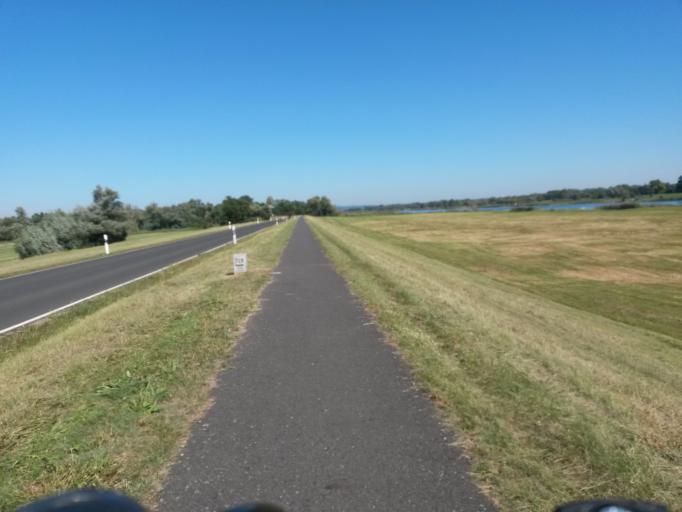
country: PL
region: West Pomeranian Voivodeship
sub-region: Powiat gryfinski
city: Cedynia
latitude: 52.8604
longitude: 14.1351
